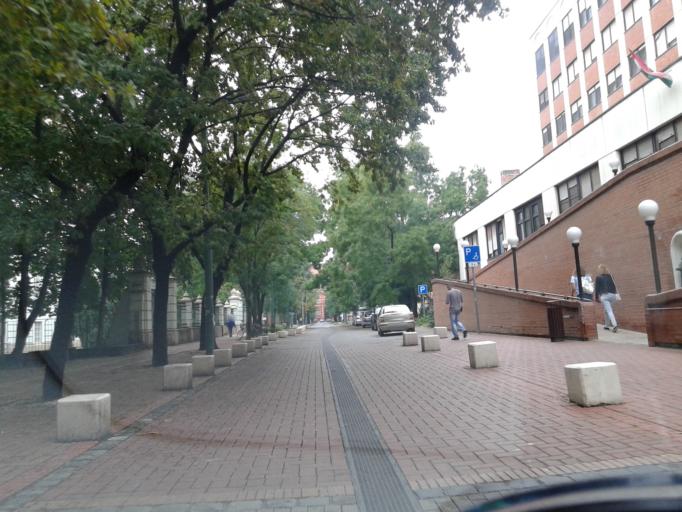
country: HU
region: Csongrad
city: Szeged
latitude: 46.2447
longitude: 20.1466
